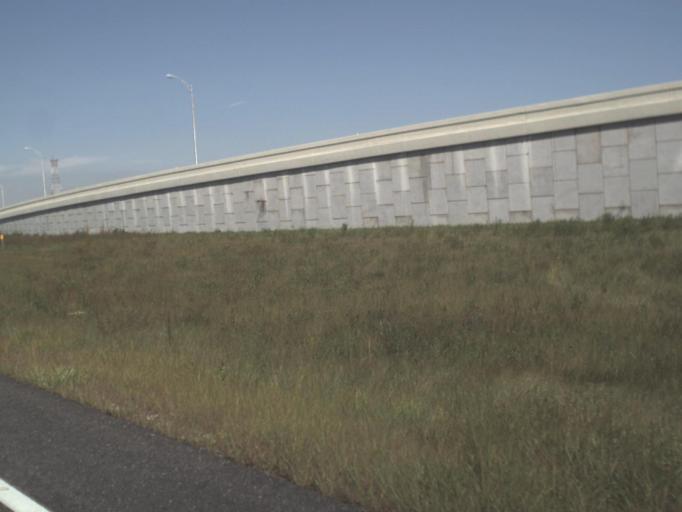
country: US
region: Florida
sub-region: Glades County
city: Moore Haven
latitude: 26.7571
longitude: -81.0827
